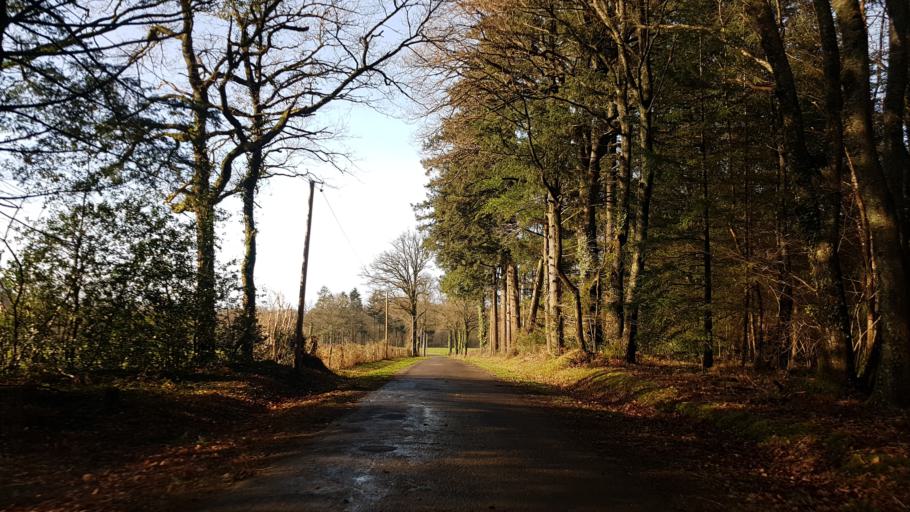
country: FR
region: Poitou-Charentes
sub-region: Departement de la Charente
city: Etagnac
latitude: 45.9085
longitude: 0.8141
